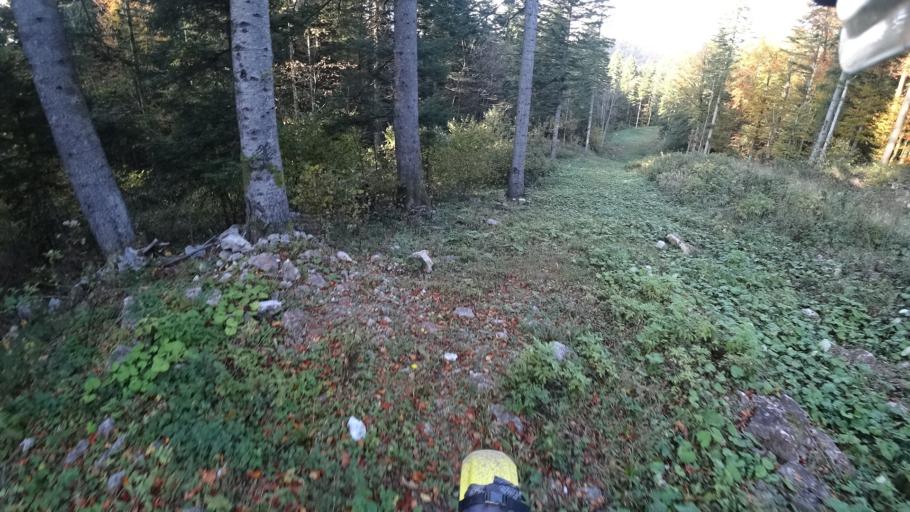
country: HR
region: Karlovacka
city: Plaski
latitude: 44.9803
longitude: 15.4022
